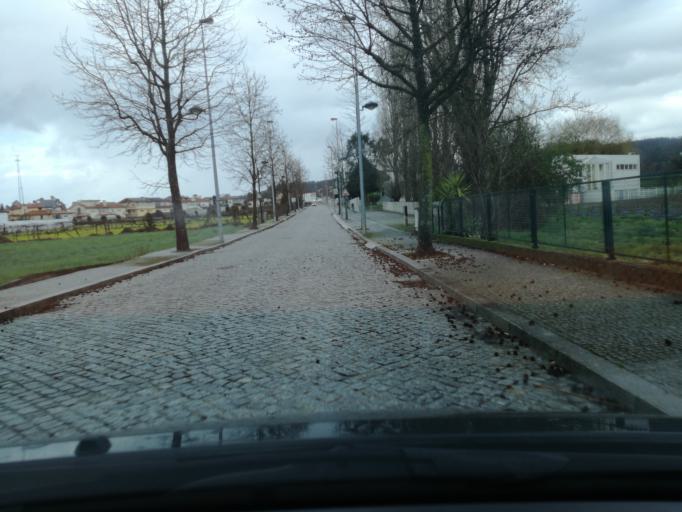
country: PT
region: Porto
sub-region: Valongo
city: Ermesinde
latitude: 41.2465
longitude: -8.5504
